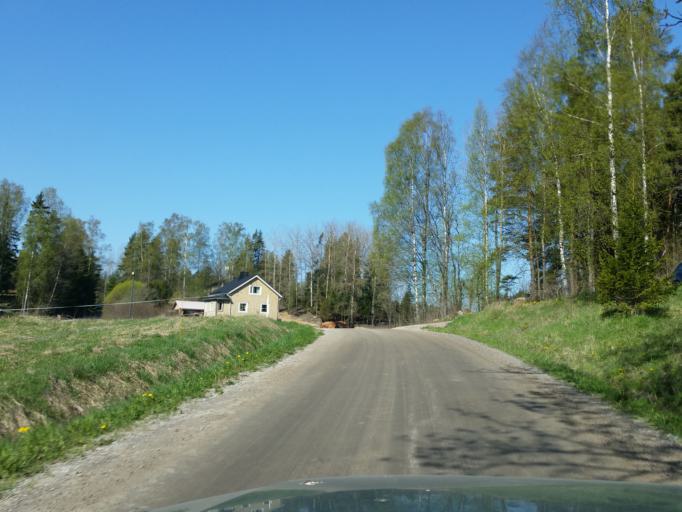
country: FI
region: Uusimaa
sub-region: Helsinki
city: Karjalohja
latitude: 60.1428
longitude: 23.7345
